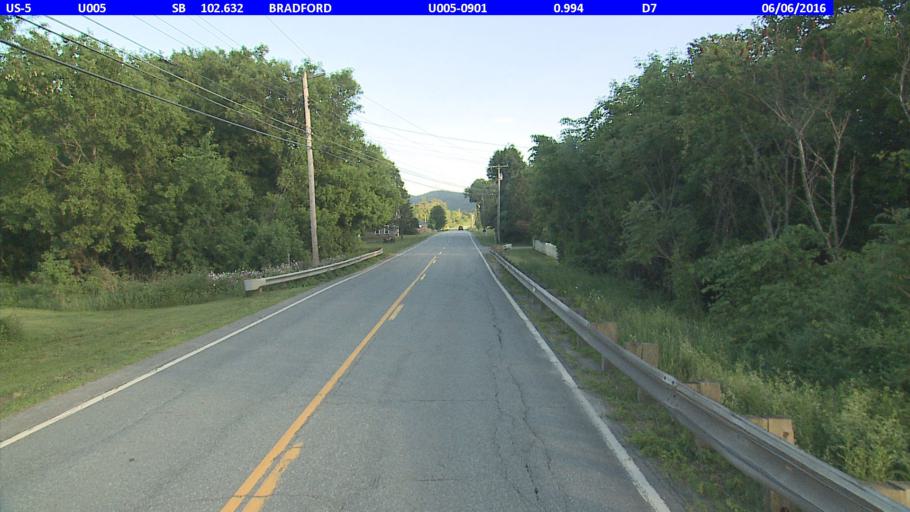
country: US
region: New Hampshire
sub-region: Grafton County
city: Orford
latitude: 43.9758
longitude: -72.1181
